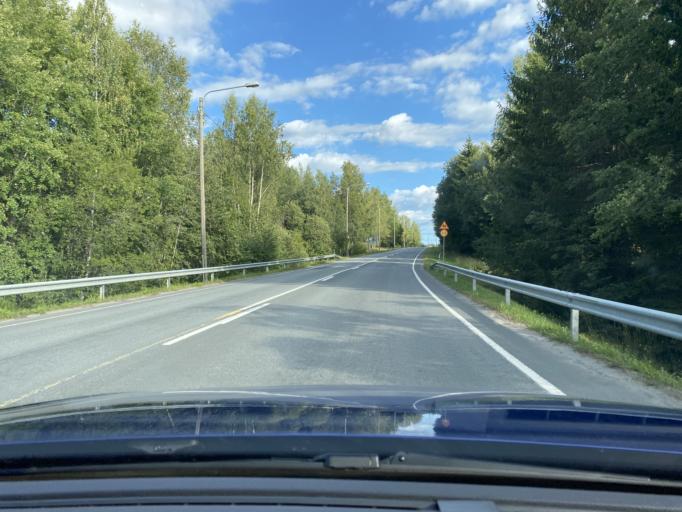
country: FI
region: Pirkanmaa
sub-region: Tampere
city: Lempaeaelae
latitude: 61.3782
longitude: 23.7791
